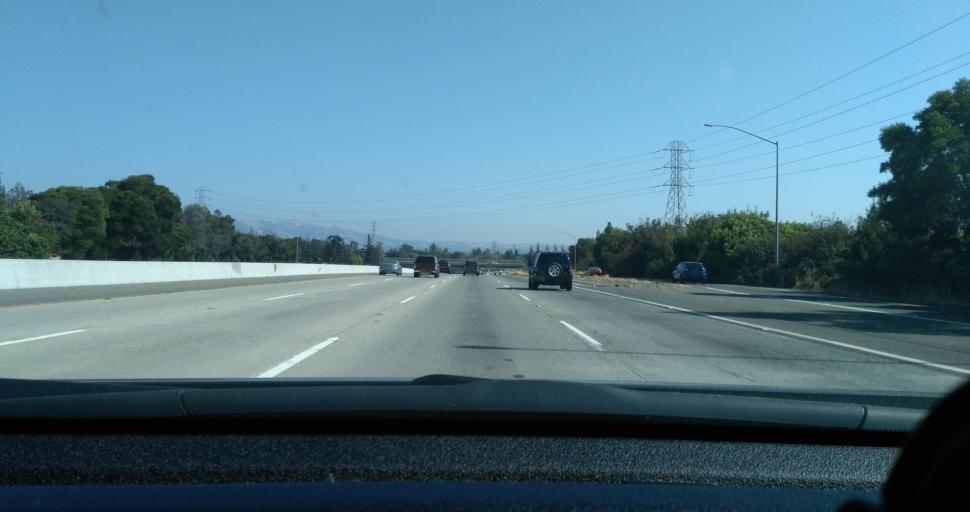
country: US
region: California
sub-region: Santa Clara County
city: Alum Rock
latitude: 37.3714
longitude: -121.8498
